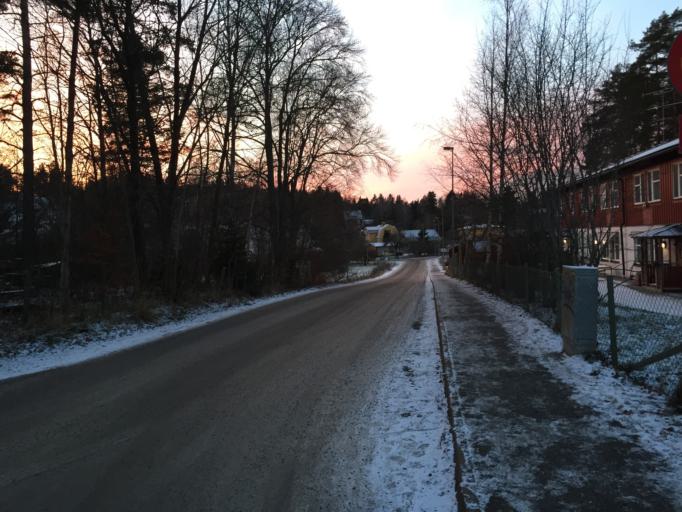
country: SE
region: Stockholm
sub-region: Salems Kommun
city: Ronninge
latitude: 59.1899
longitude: 17.7513
